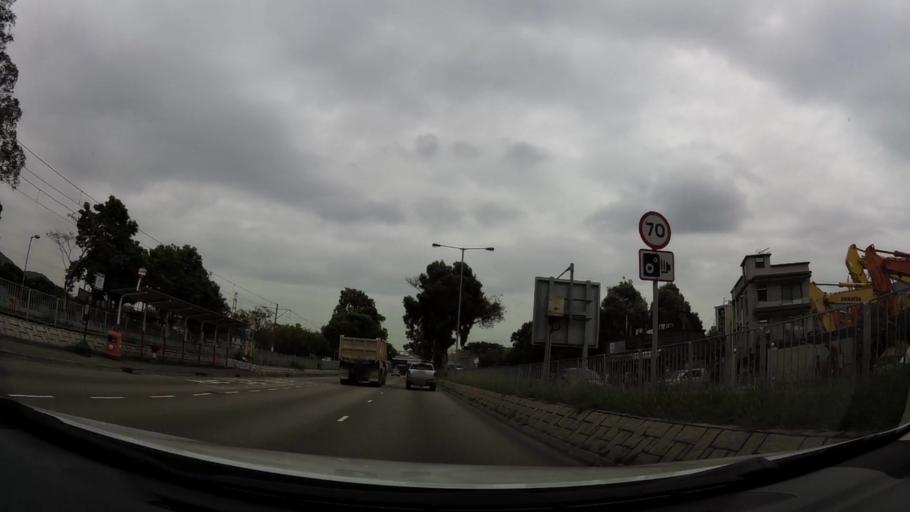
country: HK
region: Tuen Mun
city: Tuen Mun
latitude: 22.4226
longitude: 113.9856
